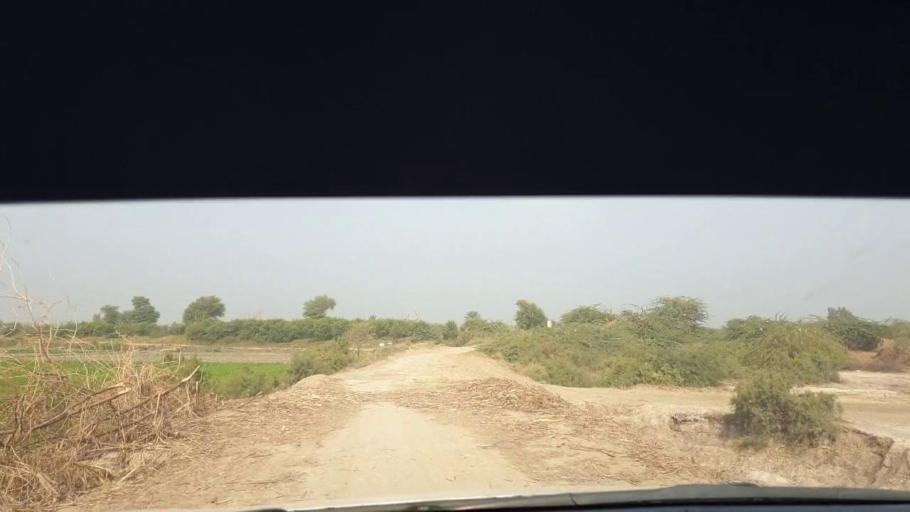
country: PK
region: Sindh
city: Berani
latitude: 25.8085
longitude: 68.8387
